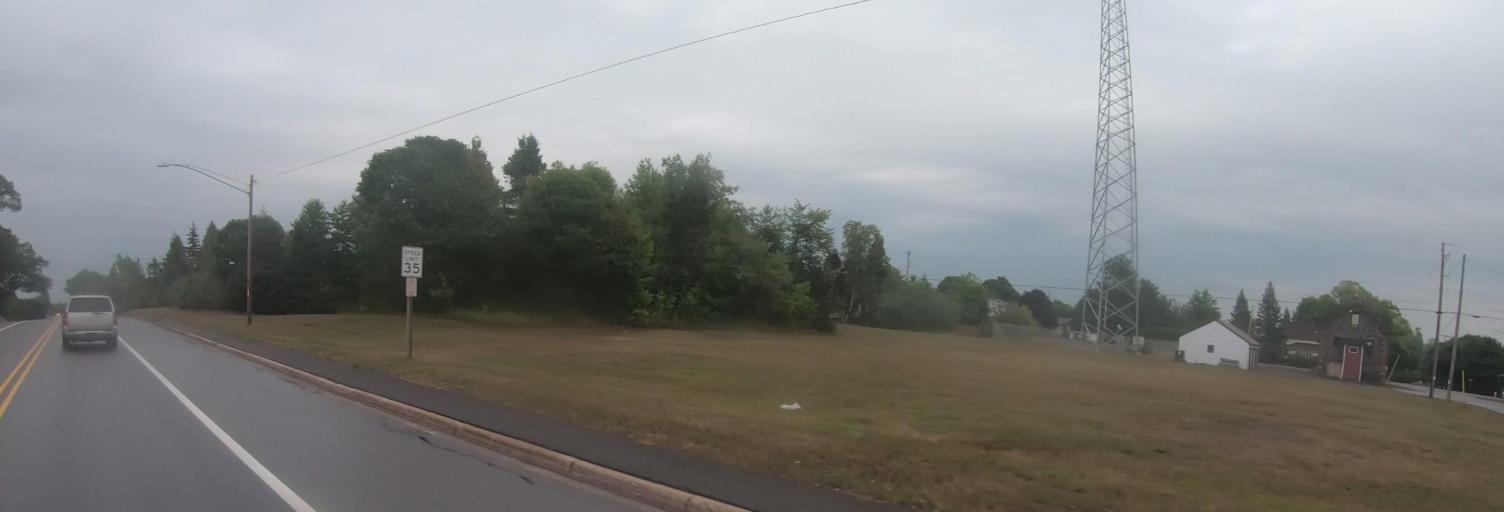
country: US
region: Michigan
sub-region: Houghton County
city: Laurium
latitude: 47.2458
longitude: -88.4438
